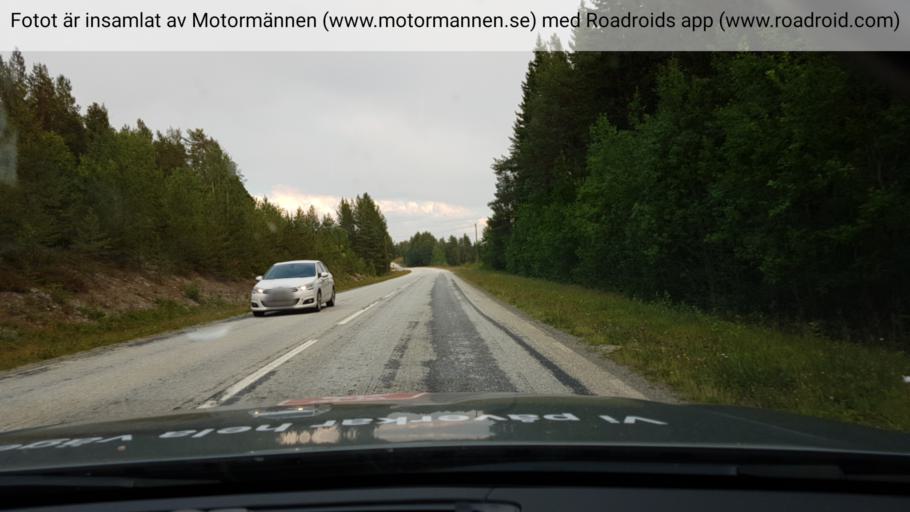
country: SE
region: Jaemtland
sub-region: Harjedalens Kommun
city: Sveg
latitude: 62.4143
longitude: 13.6318
